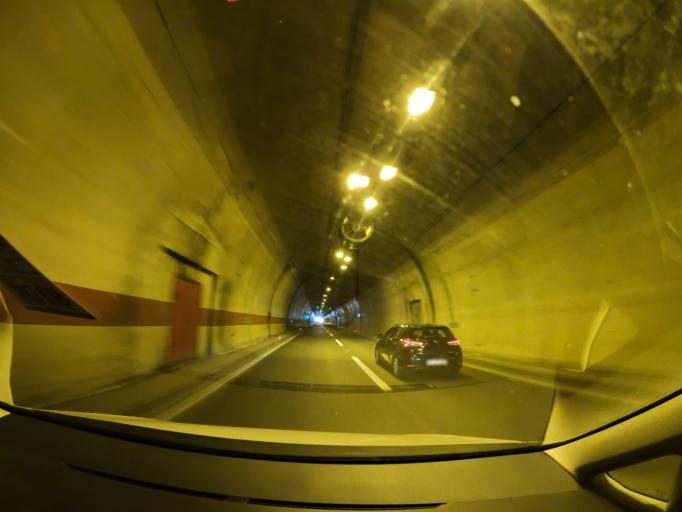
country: HR
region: Primorsko-Goranska
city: Matulji
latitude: 45.4200
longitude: 14.2539
